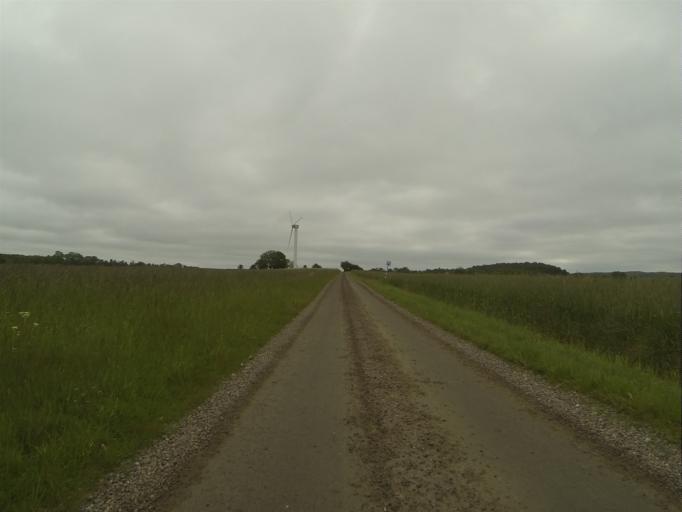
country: SE
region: Skane
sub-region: Staffanstorps Kommun
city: Staffanstorp
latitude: 55.6888
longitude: 13.3052
